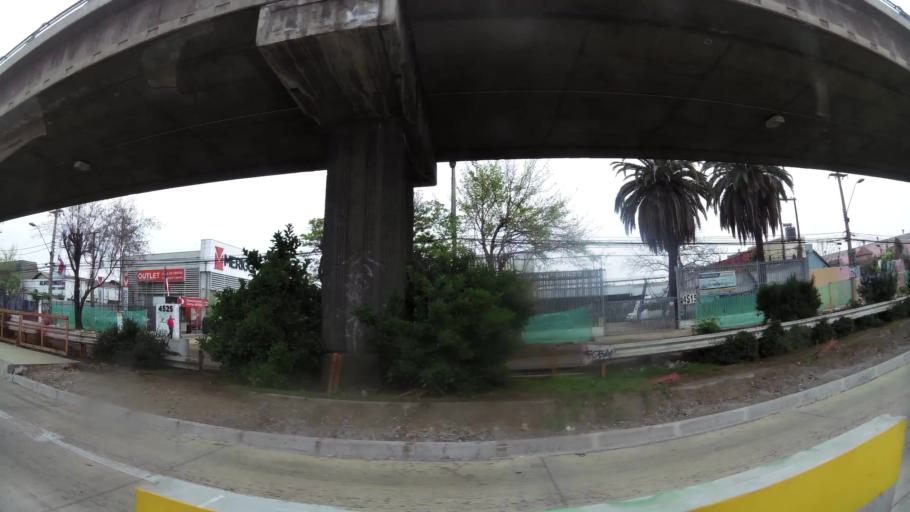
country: CL
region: Santiago Metropolitan
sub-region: Provincia de Santiago
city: Santiago
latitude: -33.4952
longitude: -70.6167
